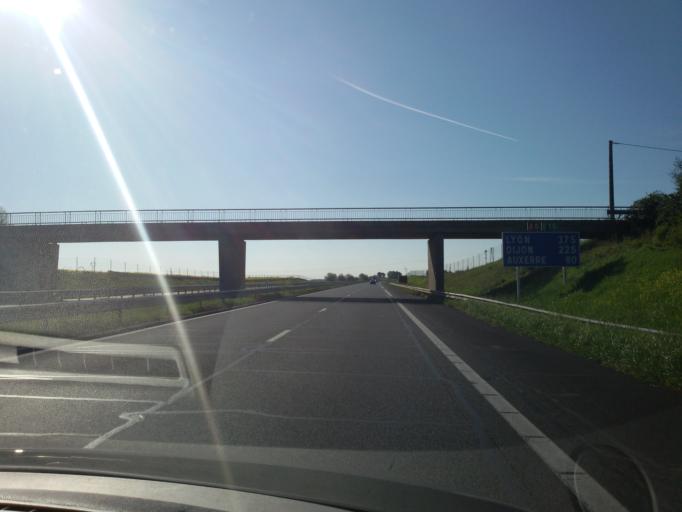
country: FR
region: Ile-de-France
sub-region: Departement de Seine-et-Marne
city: Souppes-sur-Loing
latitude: 48.2103
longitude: 2.7863
